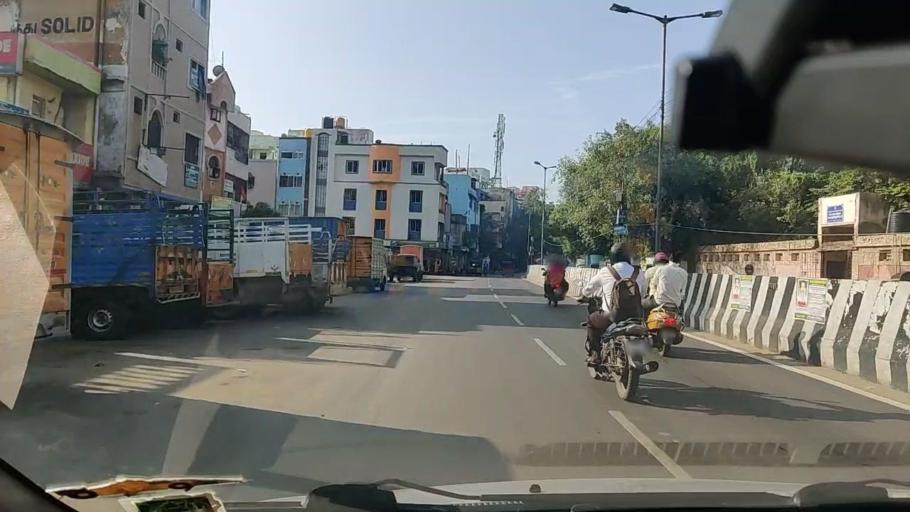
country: IN
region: Tamil Nadu
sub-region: Chennai
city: George Town
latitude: 13.1009
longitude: 80.2749
